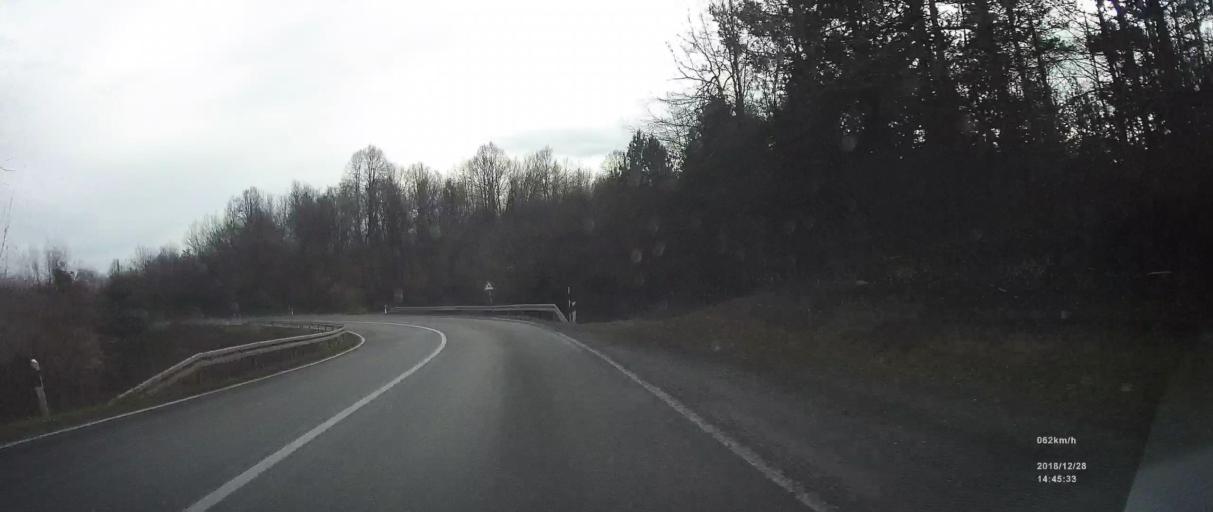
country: SI
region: Crnomelj
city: Crnomelj
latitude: 45.4518
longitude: 15.3056
